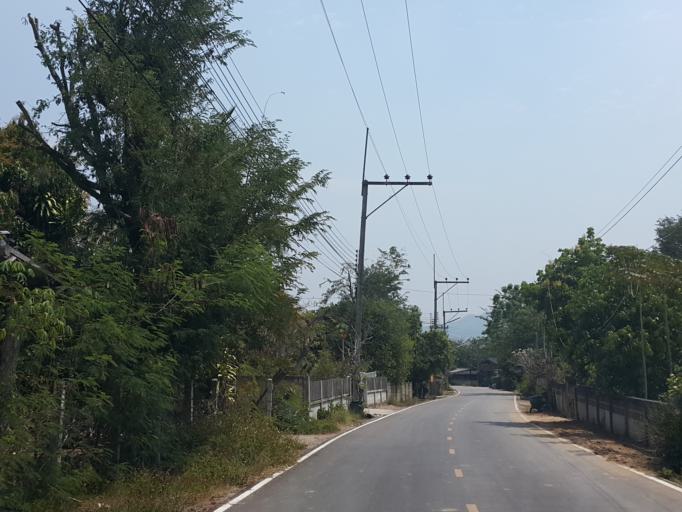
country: TH
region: Lampang
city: Mueang Pan
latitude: 18.7822
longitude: 99.5015
